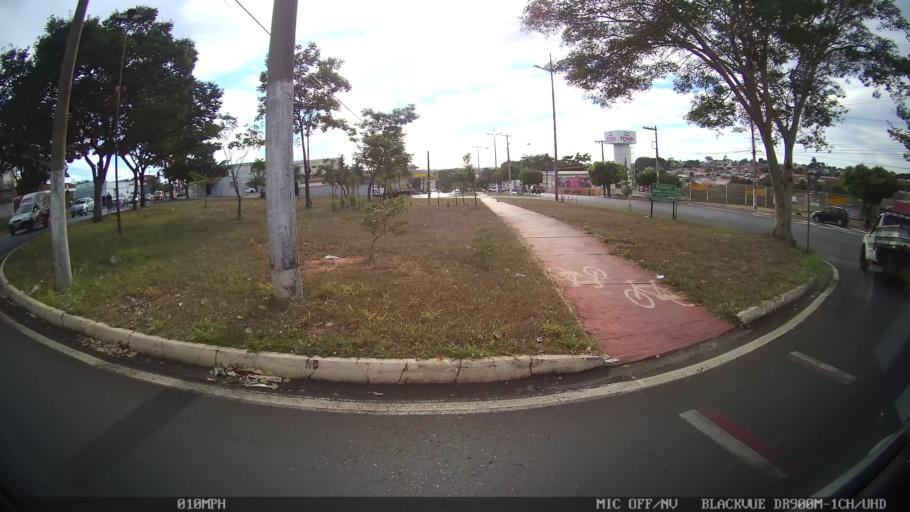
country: BR
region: Sao Paulo
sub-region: Catanduva
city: Catanduva
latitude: -21.1502
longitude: -48.9788
